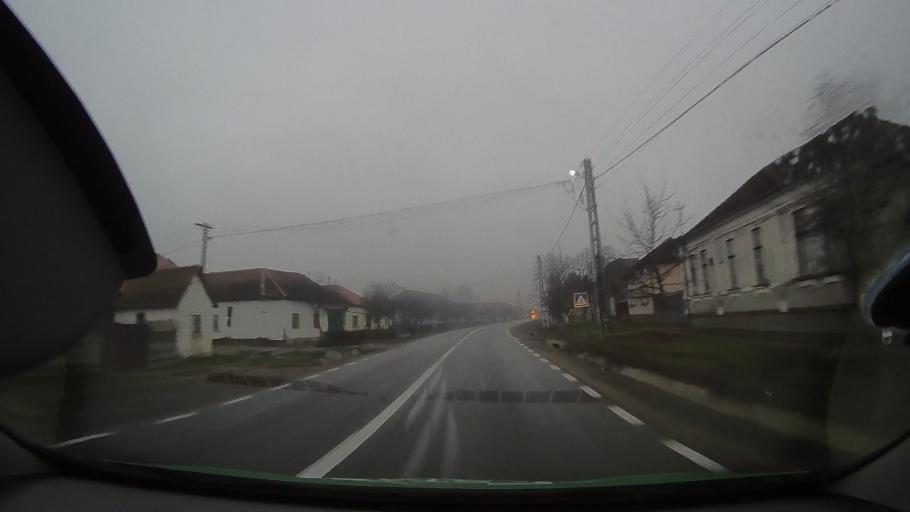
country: RO
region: Bihor
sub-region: Comuna Olcea
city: Calacea
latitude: 46.6406
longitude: 21.9557
